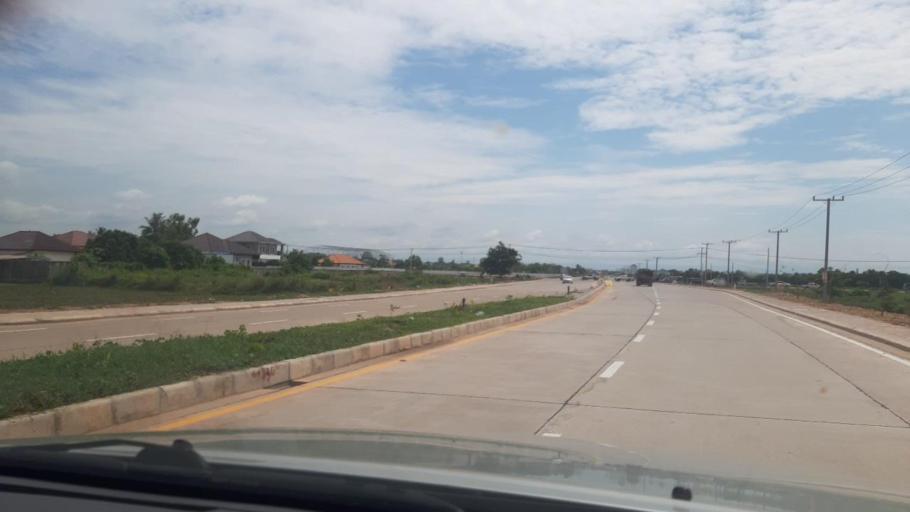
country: LA
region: Vientiane
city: Vientiane
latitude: 18.0298
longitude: 102.6080
